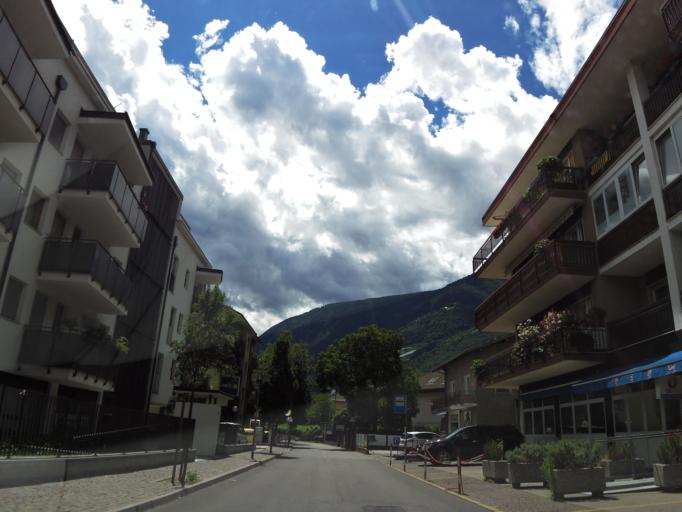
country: IT
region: Trentino-Alto Adige
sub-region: Bolzano
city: Merano
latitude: 46.6642
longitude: 11.1515
